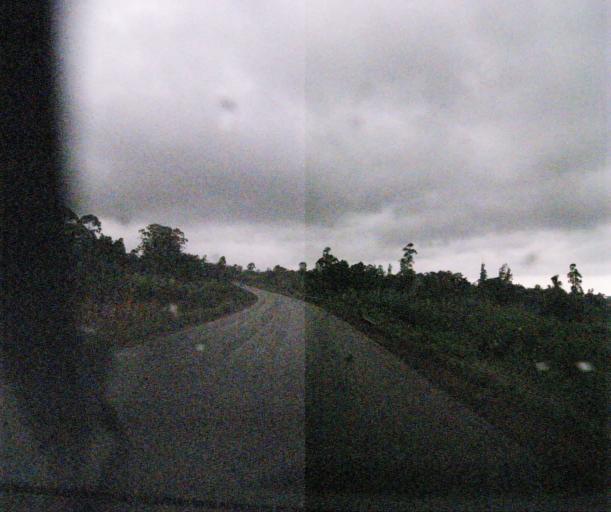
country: CM
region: West
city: Bansoa
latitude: 5.4766
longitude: 10.2806
